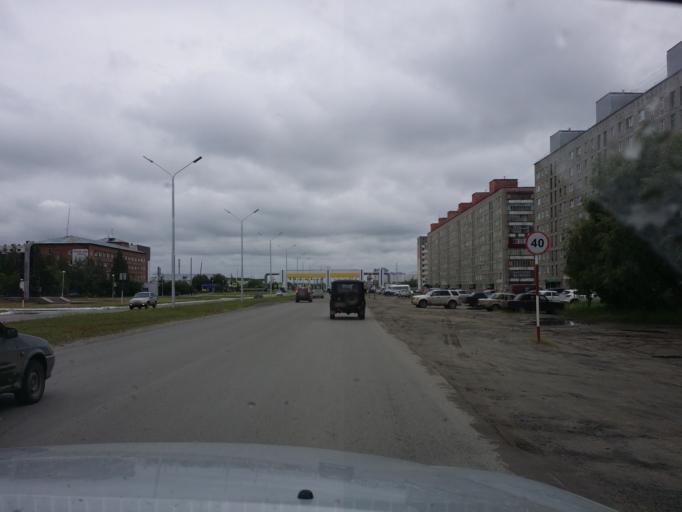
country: RU
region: Khanty-Mansiyskiy Avtonomnyy Okrug
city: Nizhnevartovsk
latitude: 60.9423
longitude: 76.6115
